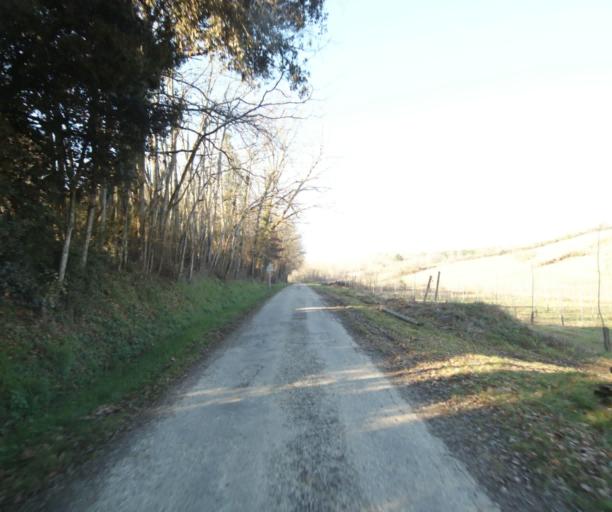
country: FR
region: Midi-Pyrenees
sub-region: Departement du Tarn-et-Garonne
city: Moissac
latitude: 44.1317
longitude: 1.0883
